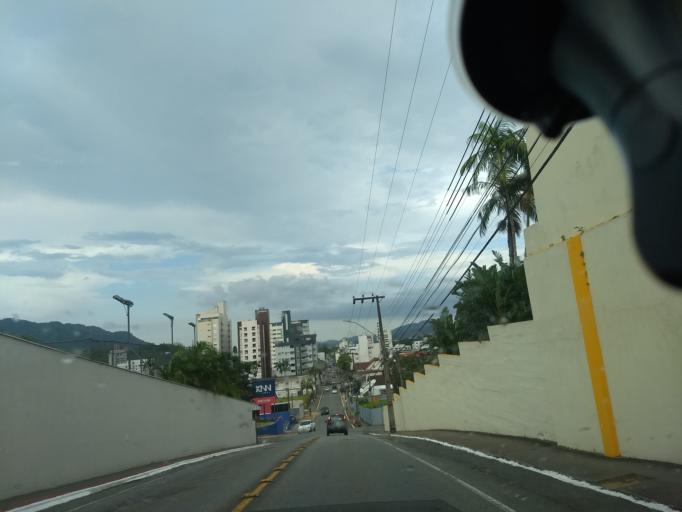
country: BR
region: Santa Catarina
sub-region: Jaragua Do Sul
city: Jaragua do Sul
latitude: -26.4836
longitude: -49.0883
